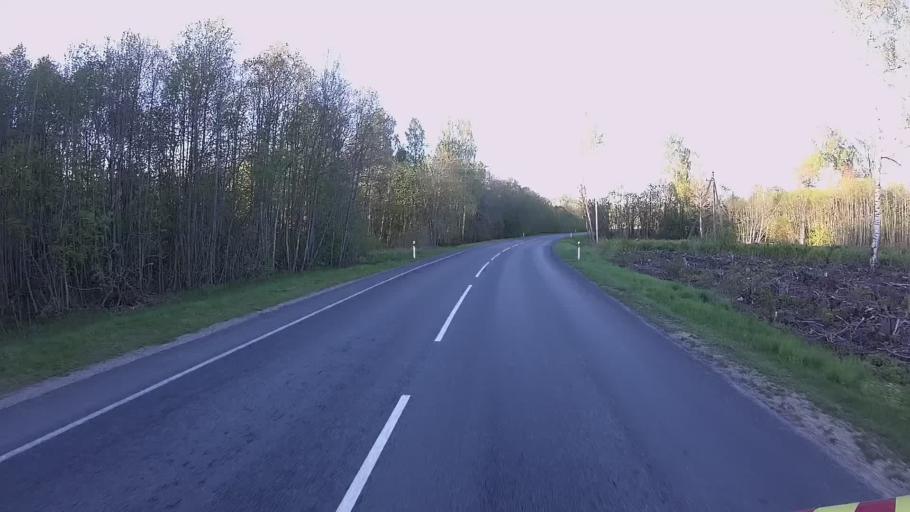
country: EE
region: Viljandimaa
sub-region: Viiratsi vald
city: Viiratsi
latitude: 58.4632
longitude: 25.7518
